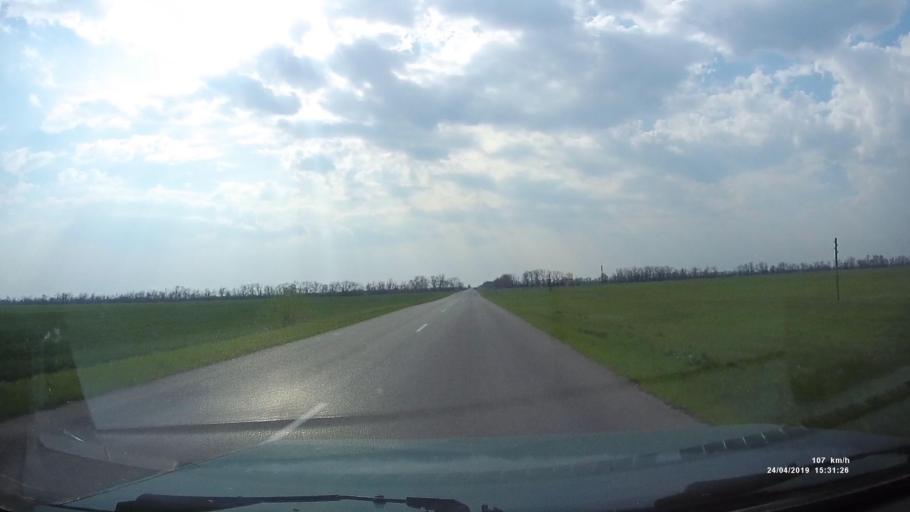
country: RU
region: Rostov
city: Remontnoye
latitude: 46.5996
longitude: 42.9834
